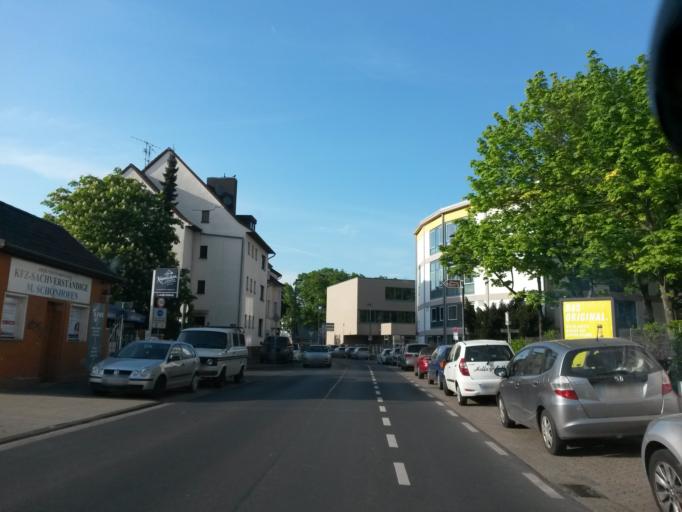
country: DE
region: North Rhine-Westphalia
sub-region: Regierungsbezirk Koln
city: Siegburg
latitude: 50.7970
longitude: 7.2028
